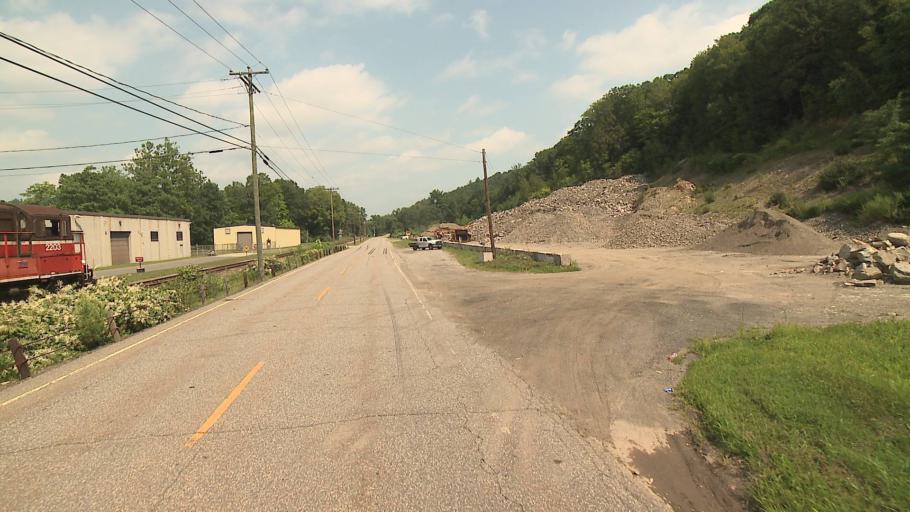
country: US
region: Connecticut
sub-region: Litchfield County
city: Thomaston
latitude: 41.6438
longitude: -73.0778
